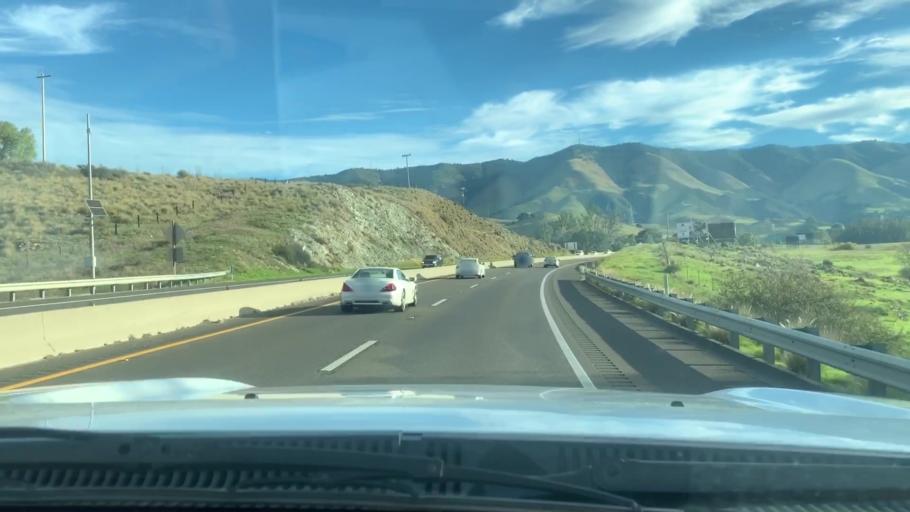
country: US
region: California
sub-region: San Luis Obispo County
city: San Luis Obispo
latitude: 35.2941
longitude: -120.6407
